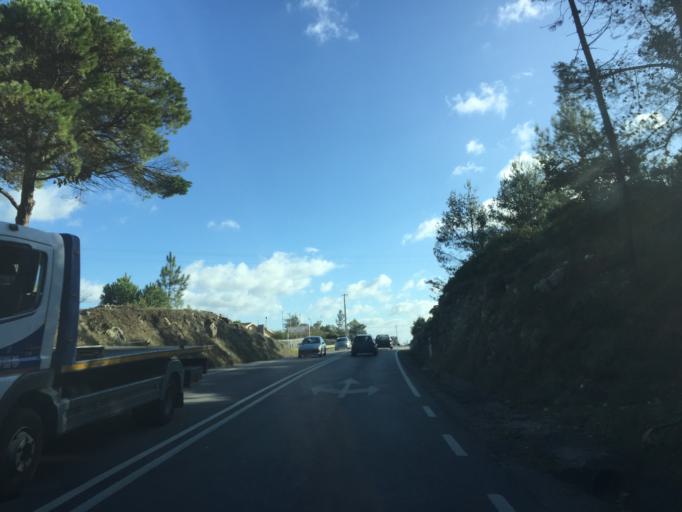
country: PT
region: Coimbra
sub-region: Figueira da Foz
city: Tavarede
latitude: 40.1916
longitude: -8.8305
